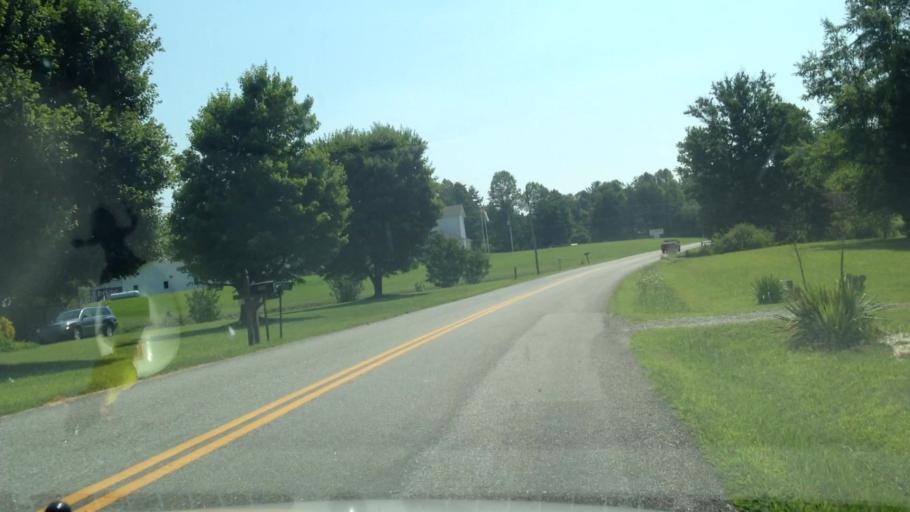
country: US
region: Virginia
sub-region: Patrick County
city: Stuart
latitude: 36.5785
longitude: -80.2491
